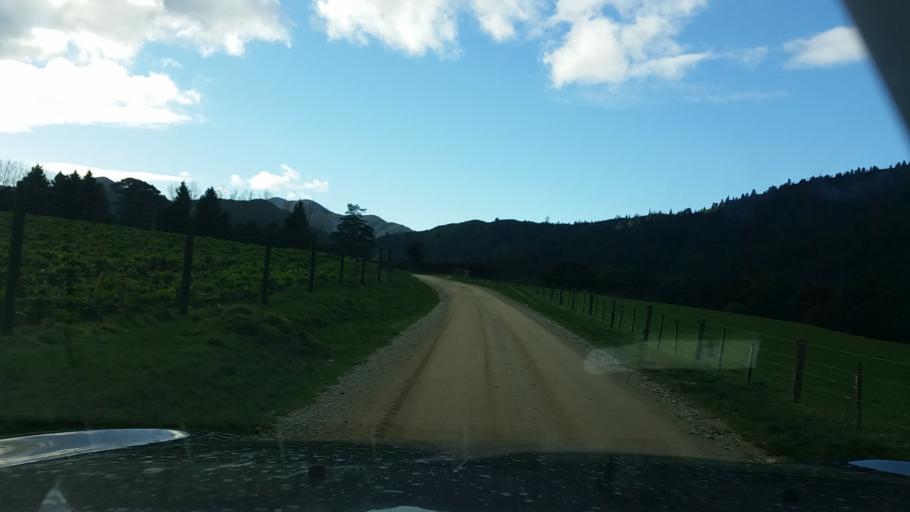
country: NZ
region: Marlborough
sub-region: Marlborough District
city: Picton
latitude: -41.1524
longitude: 174.1317
